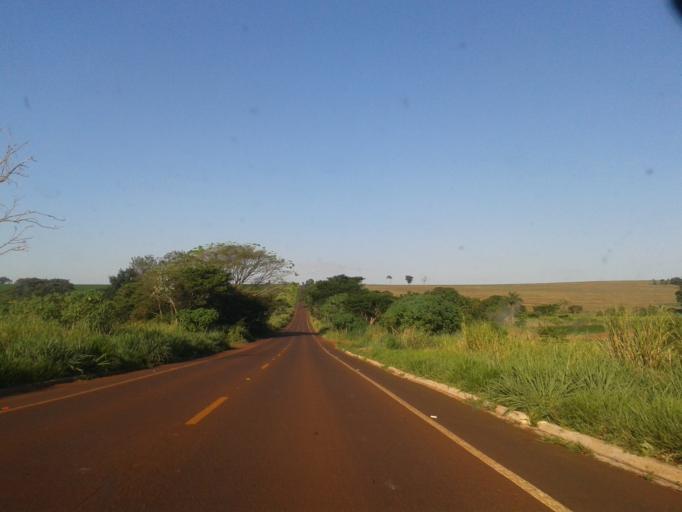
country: BR
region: Minas Gerais
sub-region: Capinopolis
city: Capinopolis
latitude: -18.7119
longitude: -49.7431
